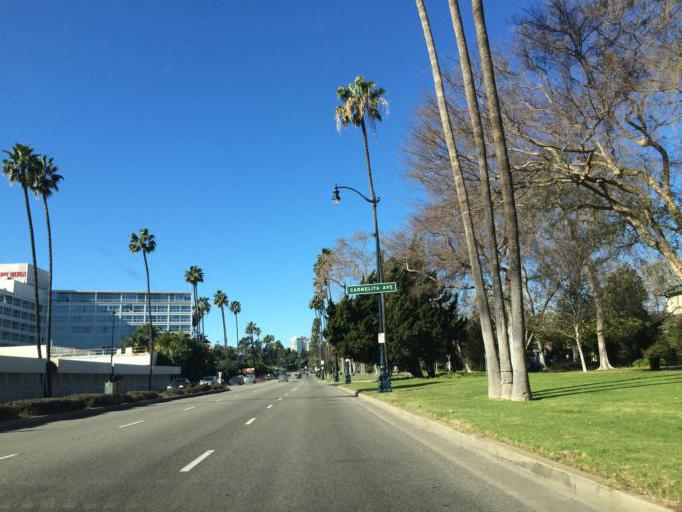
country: US
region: California
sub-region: Los Angeles County
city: Beverly Hills
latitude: 34.0672
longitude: -118.4107
